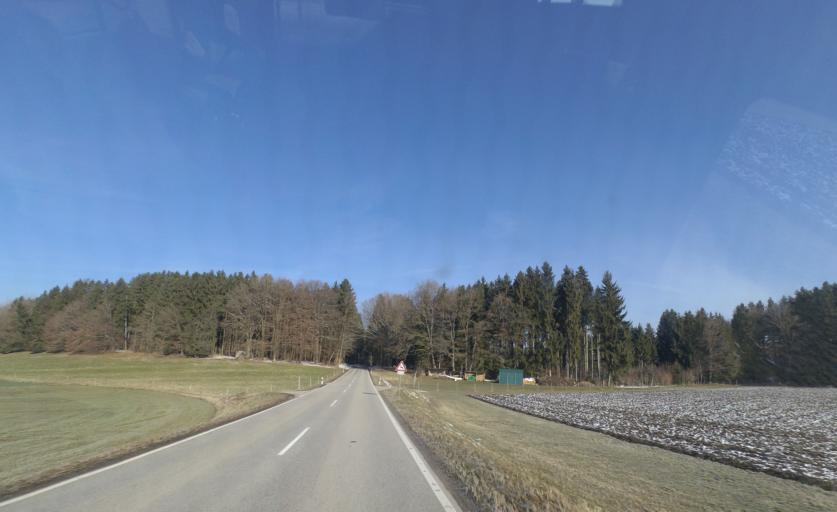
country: DE
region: Bavaria
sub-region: Upper Bavaria
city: Chieming
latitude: 47.9142
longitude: 12.5558
